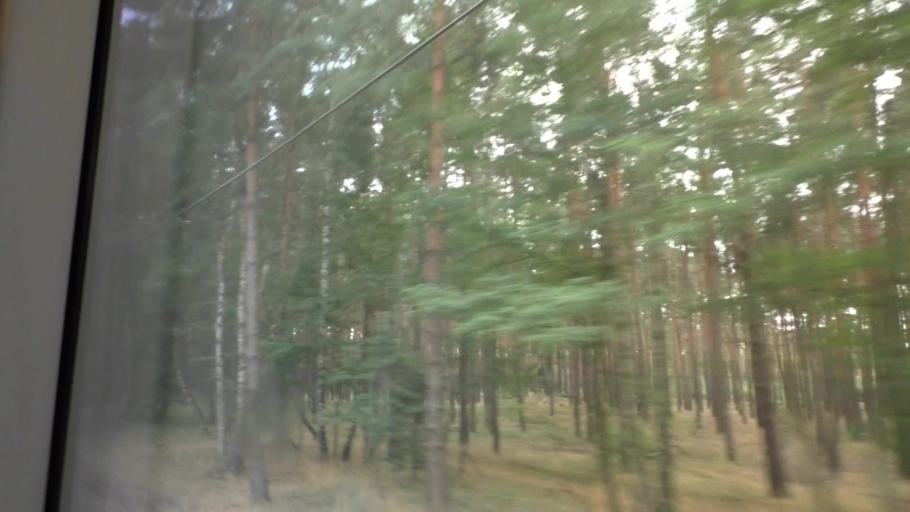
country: DE
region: Brandenburg
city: Storkow
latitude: 52.2625
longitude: 13.8991
